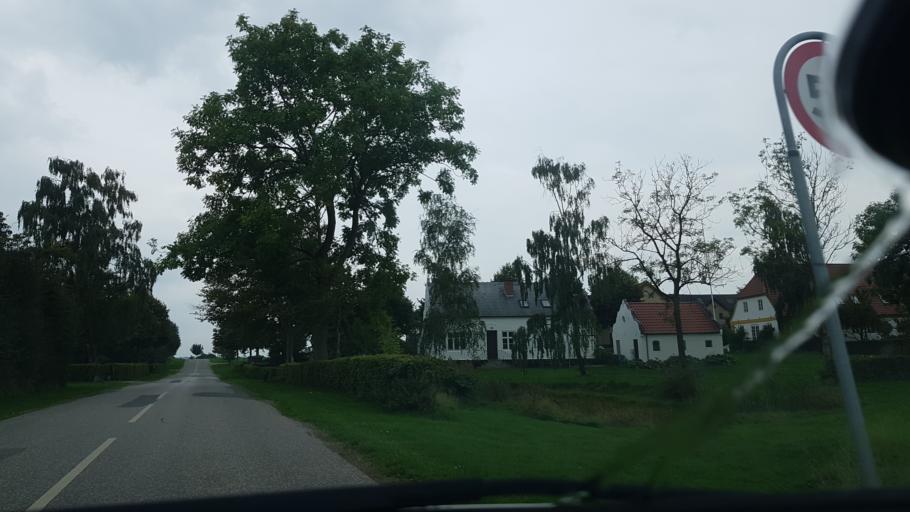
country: DK
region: South Denmark
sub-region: Kolding Kommune
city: Lunderskov
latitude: 55.5333
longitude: 9.3413
